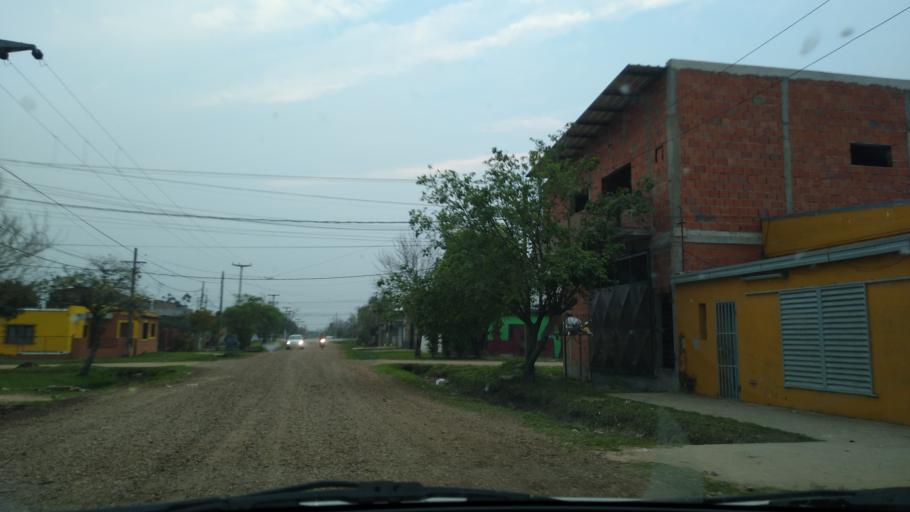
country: AR
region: Chaco
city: Barranqueras
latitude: -27.4901
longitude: -58.9546
